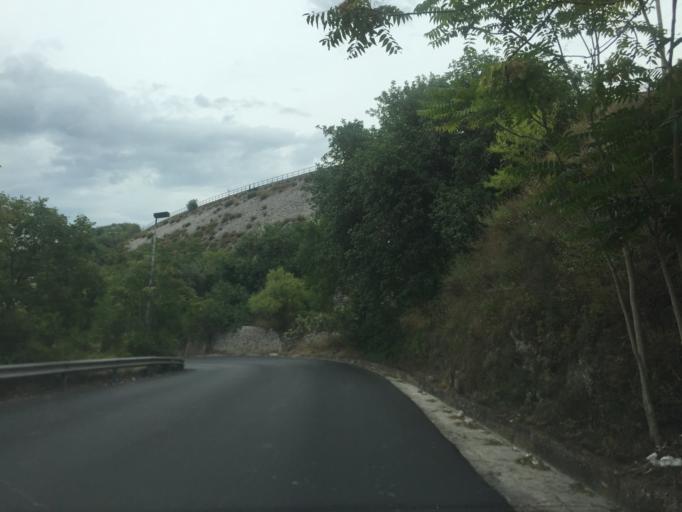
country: IT
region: Sicily
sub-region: Ragusa
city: Ragusa
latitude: 36.9198
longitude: 14.7336
